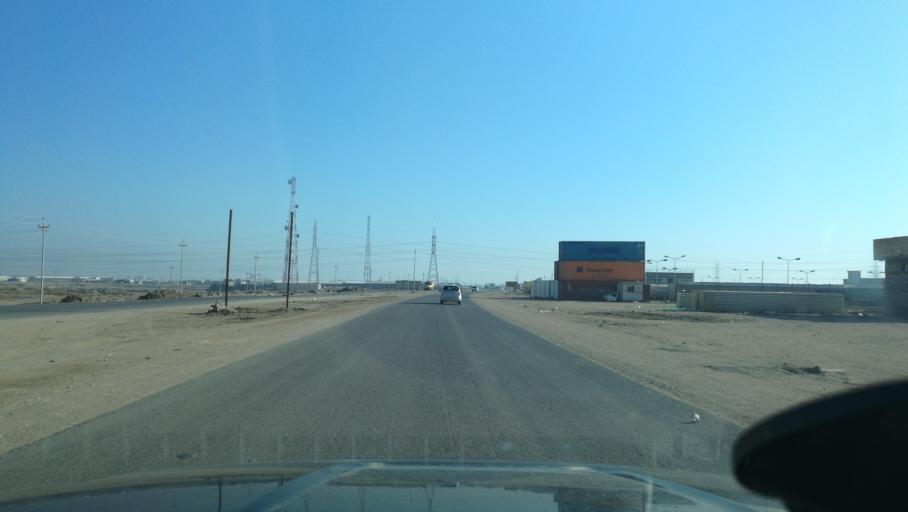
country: IQ
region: Dhi Qar
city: An Nasiriyah
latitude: 30.9970
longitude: 46.2518
